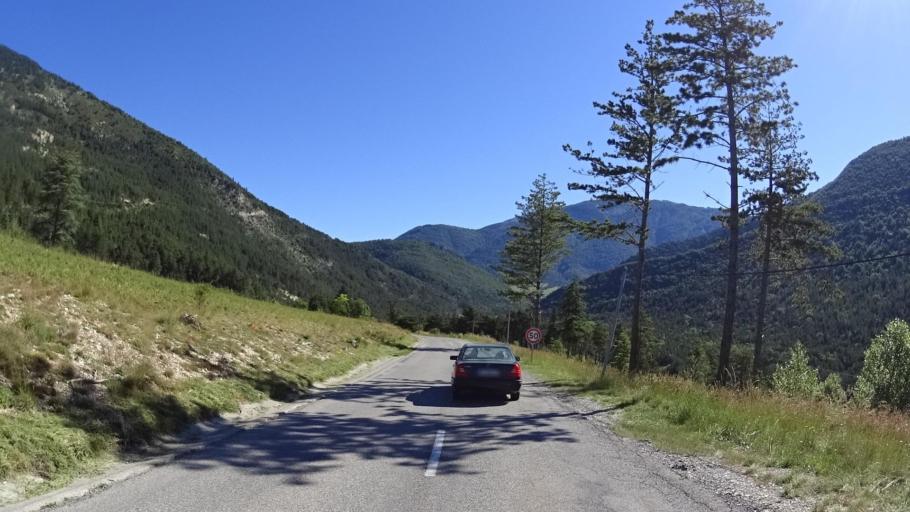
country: FR
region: Provence-Alpes-Cote d'Azur
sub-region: Departement des Alpes-de-Haute-Provence
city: Annot
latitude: 43.9939
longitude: 6.5409
